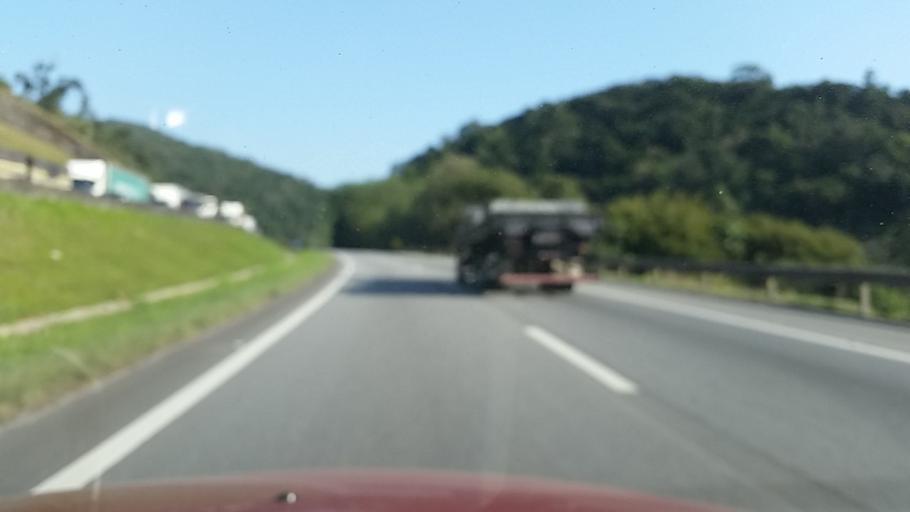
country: BR
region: Sao Paulo
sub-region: Miracatu
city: Miracatu
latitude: -24.1884
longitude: -47.3602
